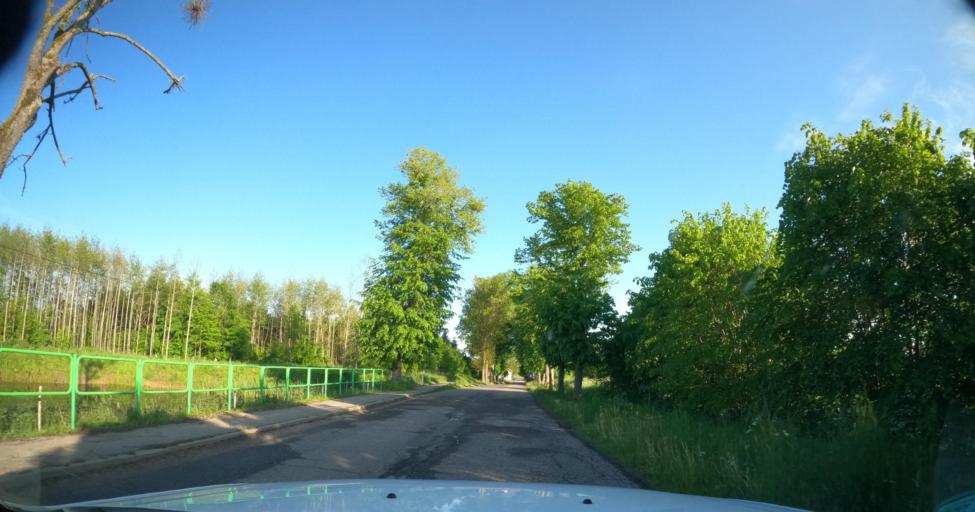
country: PL
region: Warmian-Masurian Voivodeship
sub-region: Powiat braniewski
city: Pieniezno
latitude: 54.2455
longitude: 20.0266
